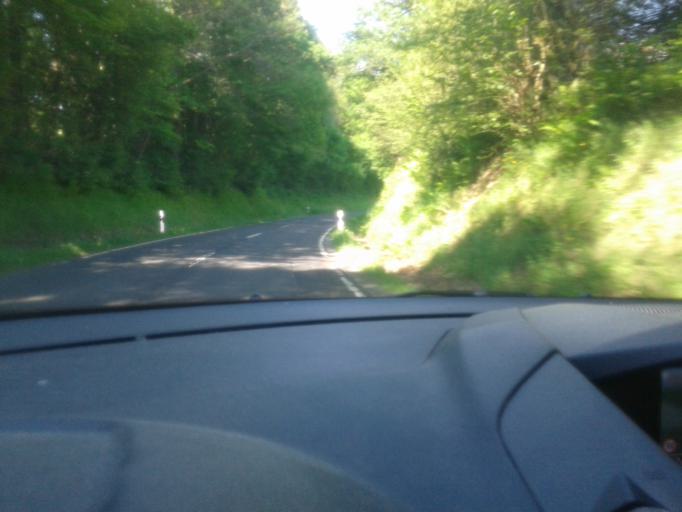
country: DE
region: Bavaria
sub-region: Regierungsbezirk Unterfranken
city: Wiesen
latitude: 50.1079
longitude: 9.3538
